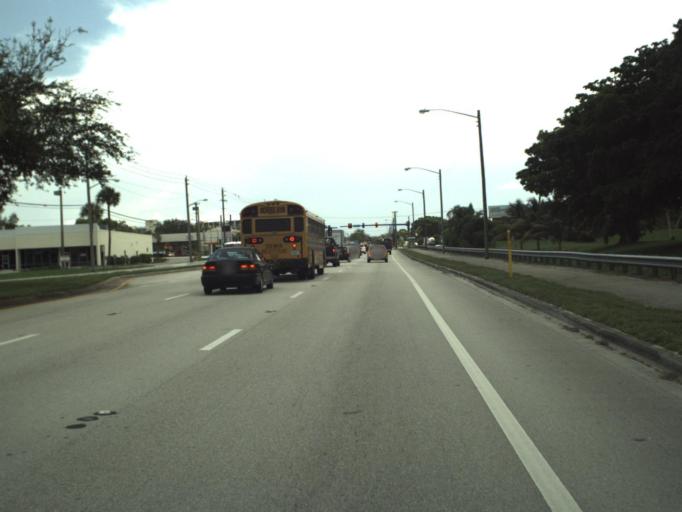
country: US
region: Florida
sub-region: Palm Beach County
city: Greenacres City
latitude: 26.6175
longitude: -80.1601
